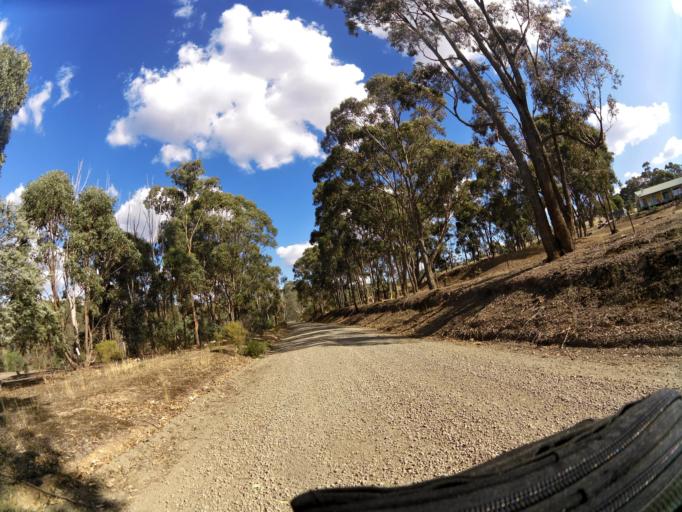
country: AU
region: Victoria
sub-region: Greater Bendigo
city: Kennington
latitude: -36.9585
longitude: 144.7805
